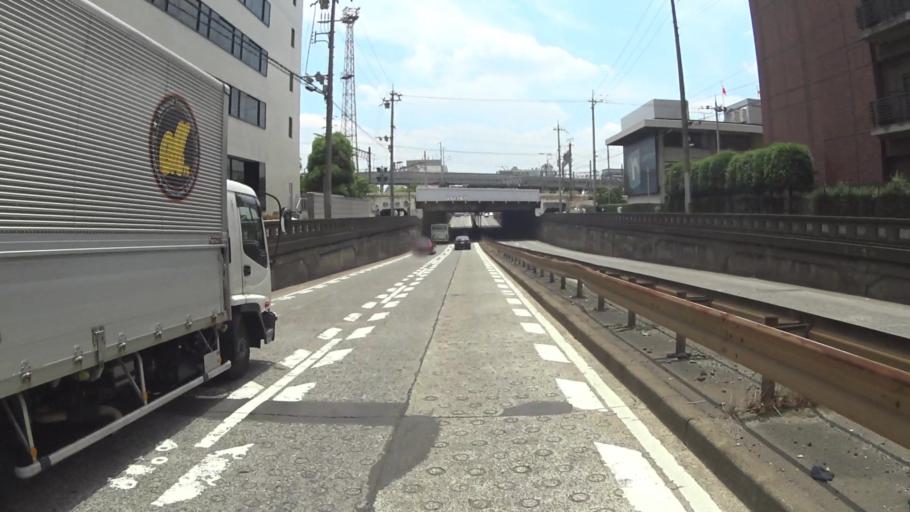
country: JP
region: Kyoto
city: Muko
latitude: 34.9831
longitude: 135.7327
